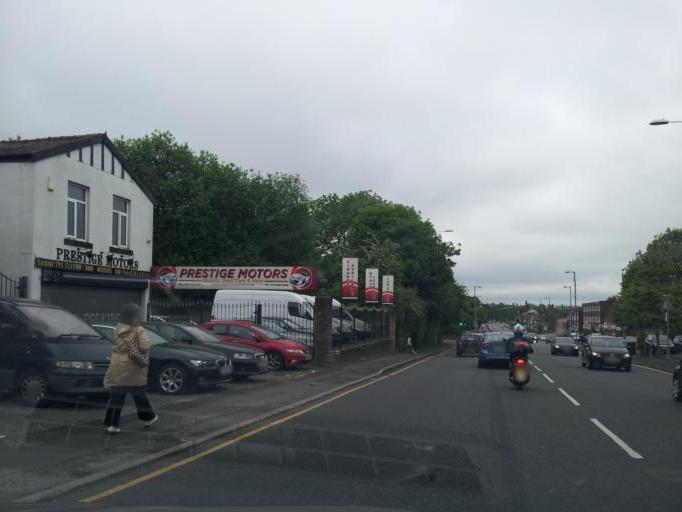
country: GB
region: England
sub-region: Manchester
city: Crumpsall
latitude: 53.5249
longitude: -2.2486
